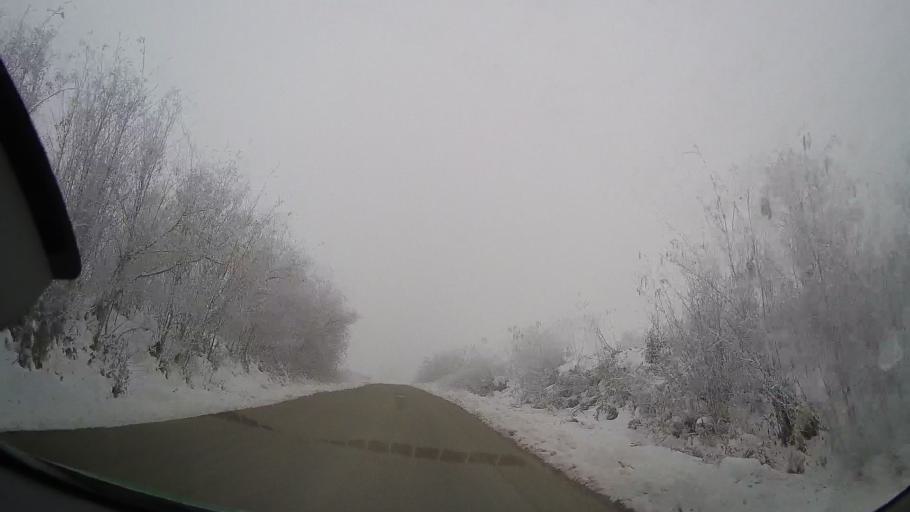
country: RO
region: Iasi
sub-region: Comuna Tansa
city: Suhulet
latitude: 46.8865
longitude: 27.2716
